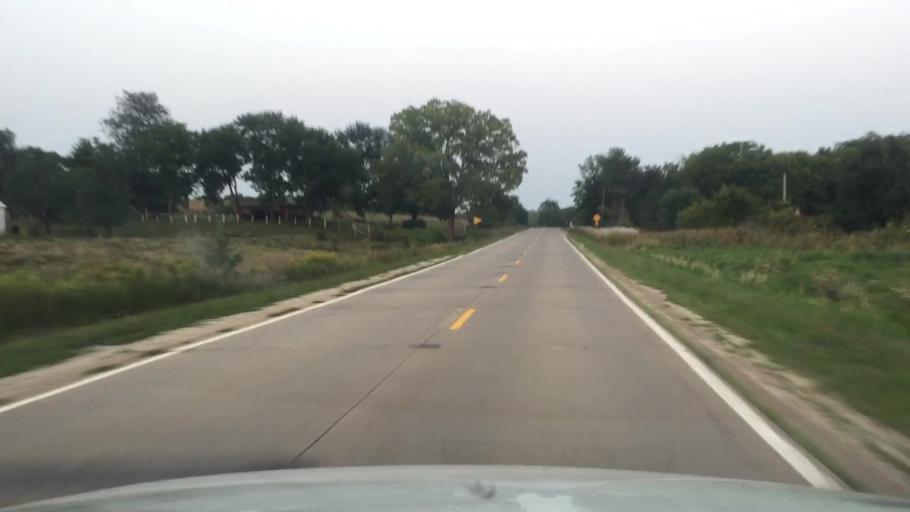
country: US
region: Iowa
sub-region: Clarke County
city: Osceola
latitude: 41.1802
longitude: -93.7176
